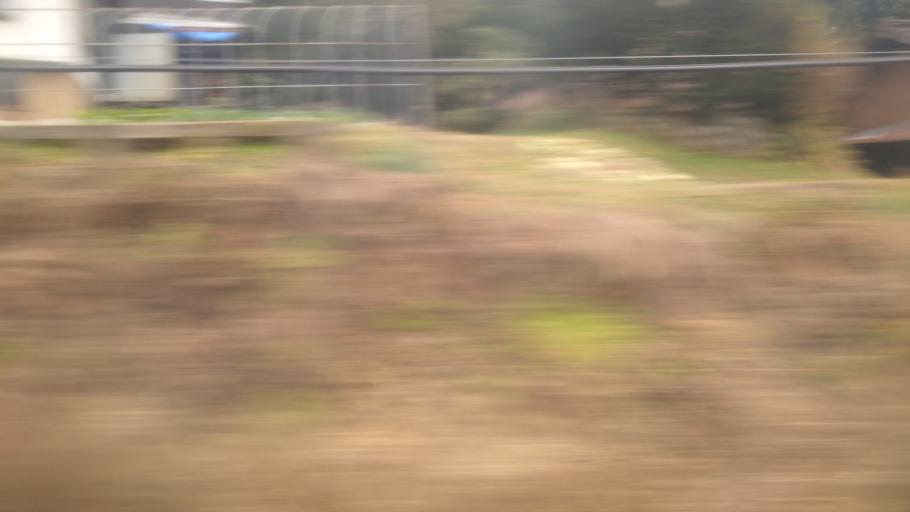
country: JP
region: Nagano
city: Iida
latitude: 35.6860
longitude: 137.6665
